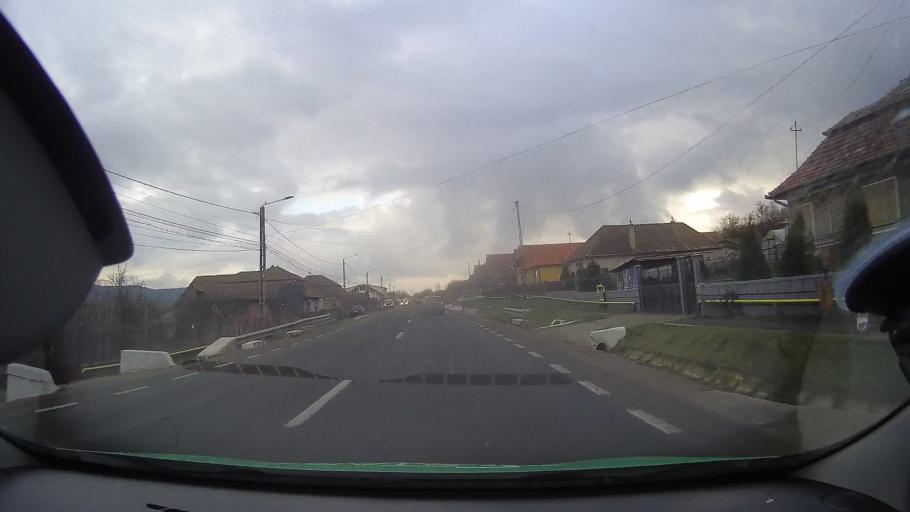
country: RO
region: Cluj
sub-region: Comuna Viisoara
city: Viisoara
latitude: 46.5135
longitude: 23.9178
